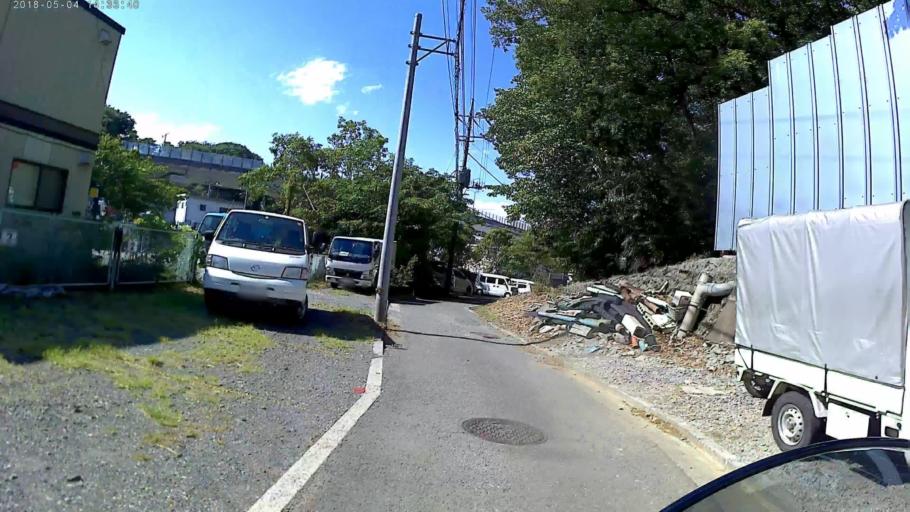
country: JP
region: Kanagawa
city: Yokohama
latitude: 35.4901
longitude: 139.5993
